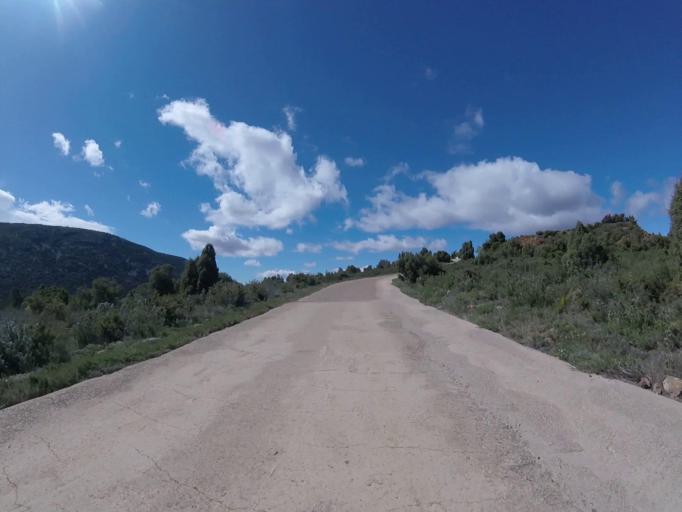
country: ES
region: Valencia
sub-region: Provincia de Castello
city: Culla
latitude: 40.3110
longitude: -0.0972
